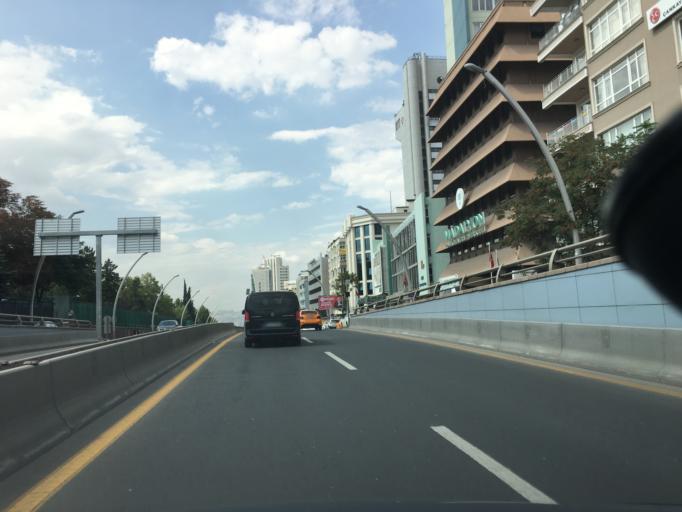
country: TR
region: Ankara
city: Cankaya
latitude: 39.9032
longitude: 32.8590
